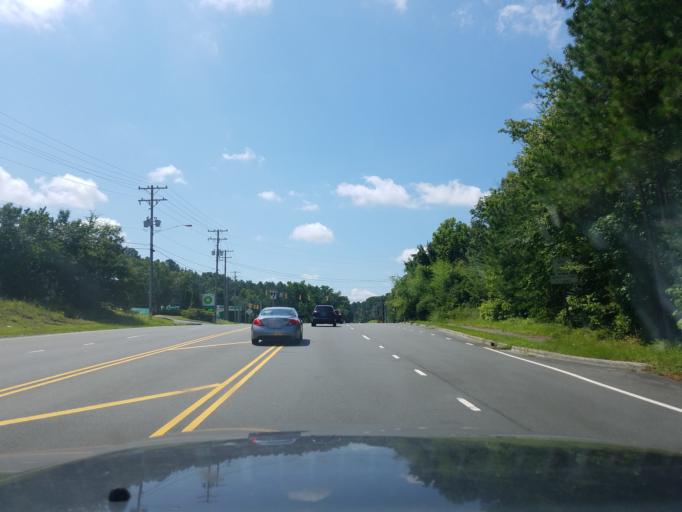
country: US
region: North Carolina
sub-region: Durham County
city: Durham
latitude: 35.9496
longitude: -78.9696
